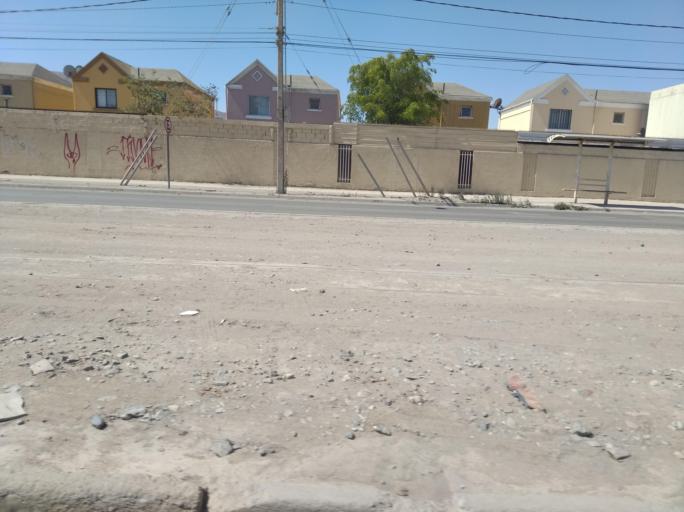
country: CL
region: Atacama
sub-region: Provincia de Copiapo
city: Copiapo
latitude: -27.3998
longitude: -70.2934
